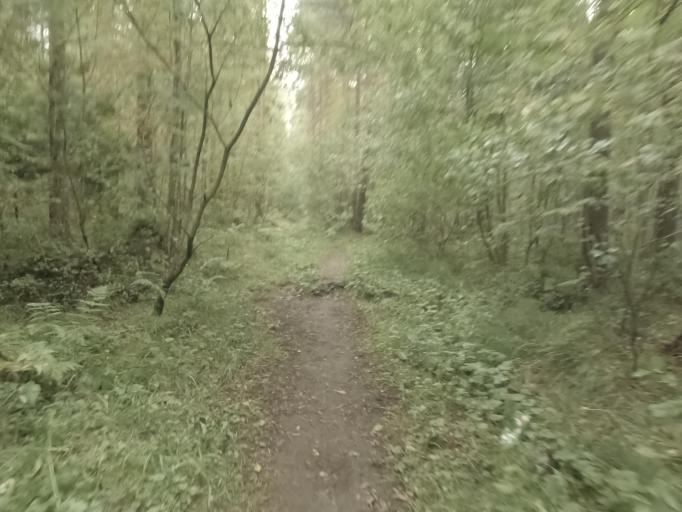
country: RU
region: St.-Petersburg
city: Krasnogvargeisky
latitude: 59.9656
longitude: 30.5115
